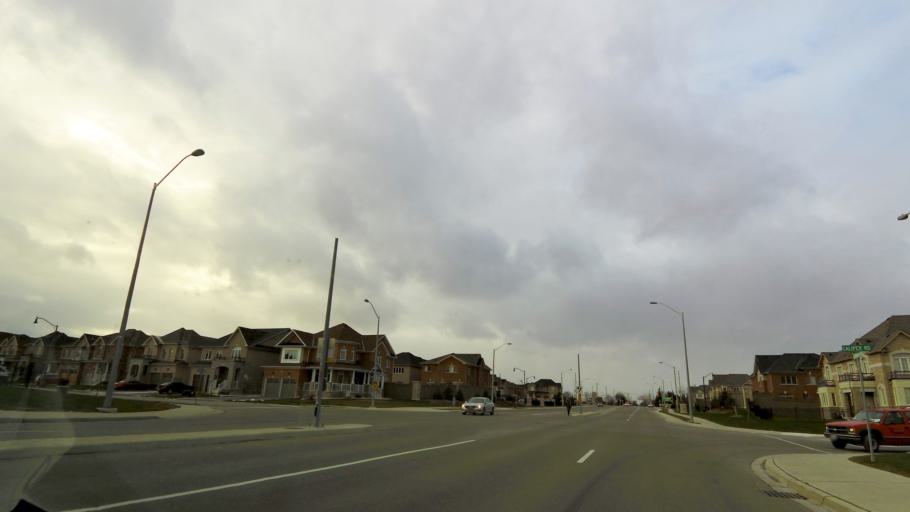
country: CA
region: Ontario
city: Brampton
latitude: 43.7982
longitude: -79.6748
